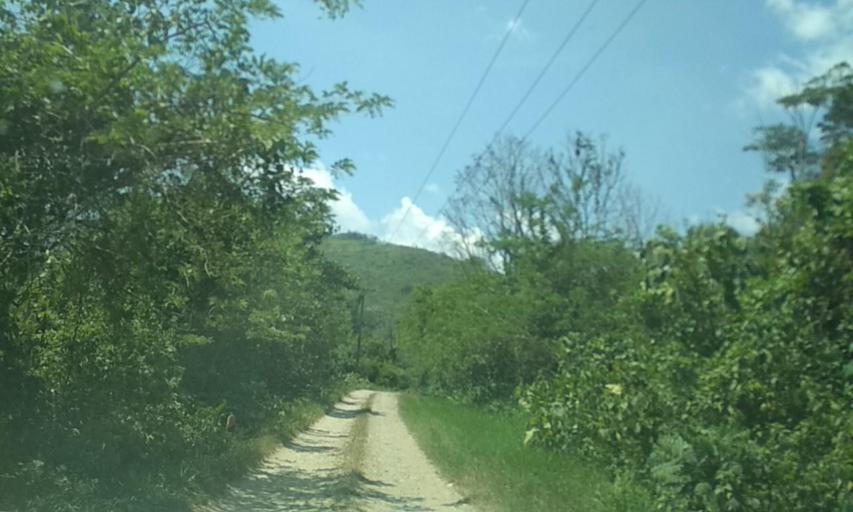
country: MX
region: Chiapas
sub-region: Tecpatan
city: Raudales Malpaso
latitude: 17.2896
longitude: -93.8424
